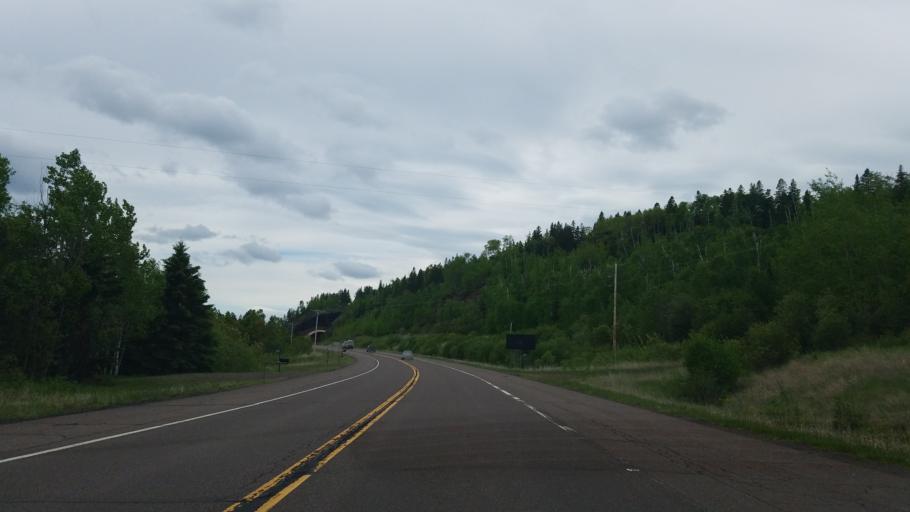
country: US
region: Minnesota
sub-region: Lake County
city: Two Harbors
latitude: 47.1007
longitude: -91.5463
